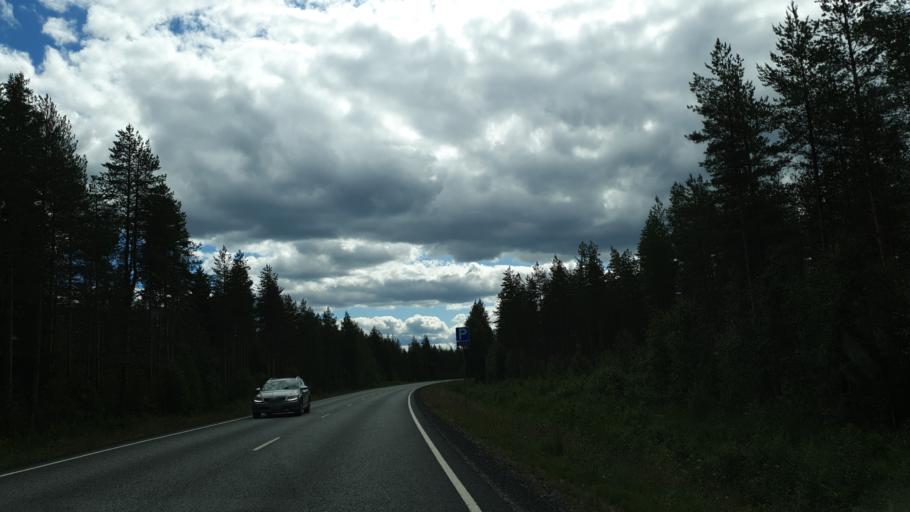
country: FI
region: Kainuu
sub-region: Kehys-Kainuu
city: Kuhmo
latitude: 64.0628
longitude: 29.5317
